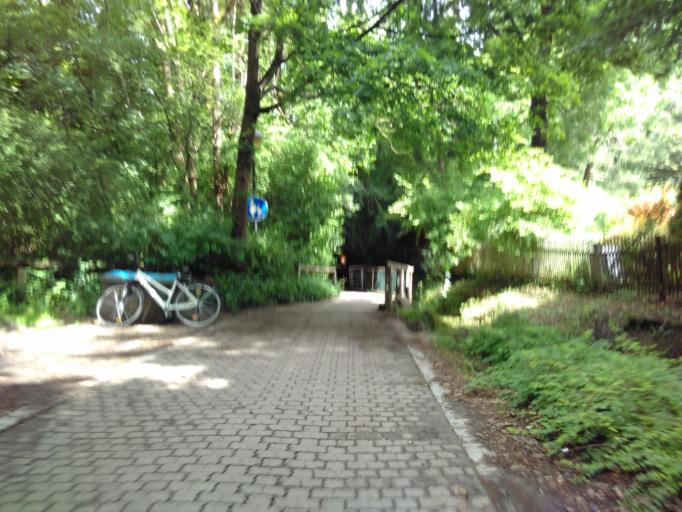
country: DE
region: Bavaria
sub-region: Upper Bavaria
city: Grobenzell
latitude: 48.2034
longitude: 11.3637
